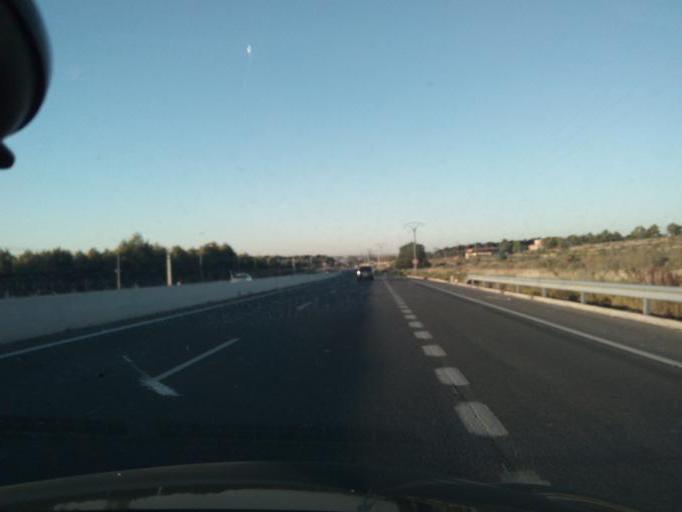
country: ES
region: Madrid
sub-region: Provincia de Madrid
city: Ajalvir
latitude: 40.4956
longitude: -3.4790
